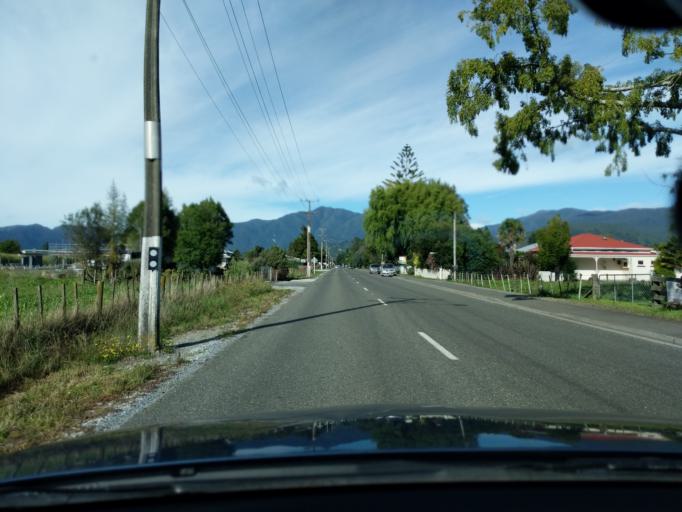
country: NZ
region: Tasman
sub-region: Tasman District
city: Takaka
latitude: -40.8567
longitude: 172.8123
